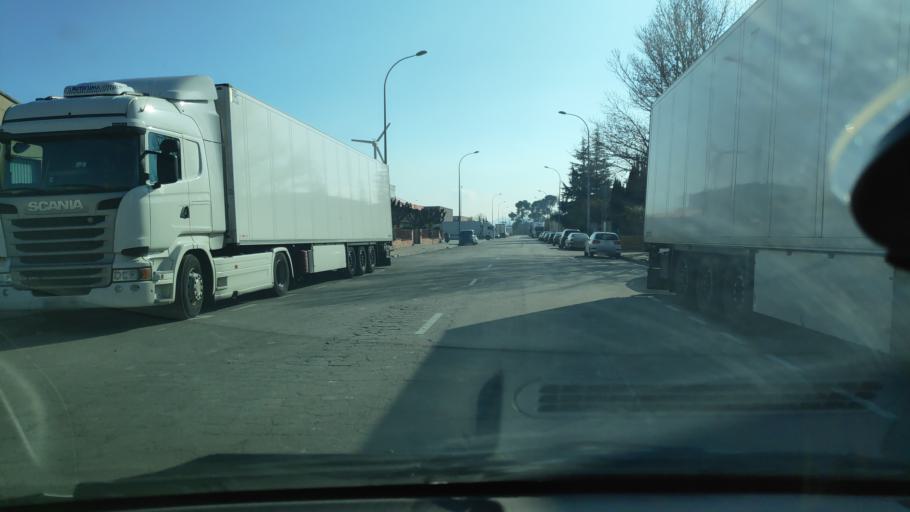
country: ES
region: Catalonia
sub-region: Provincia de Barcelona
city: Sant Quirze del Valles
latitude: 41.5225
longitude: 2.0919
